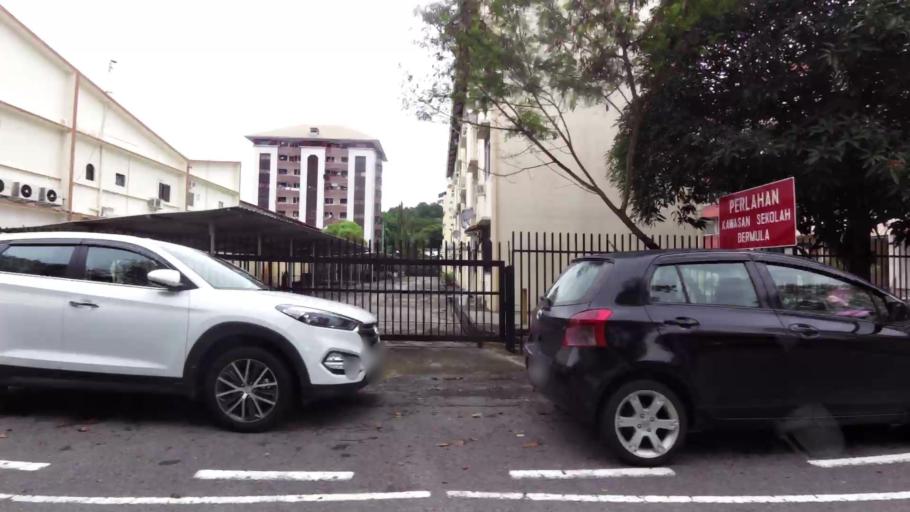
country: BN
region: Brunei and Muara
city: Bandar Seri Begawan
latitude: 4.8961
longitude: 114.9390
